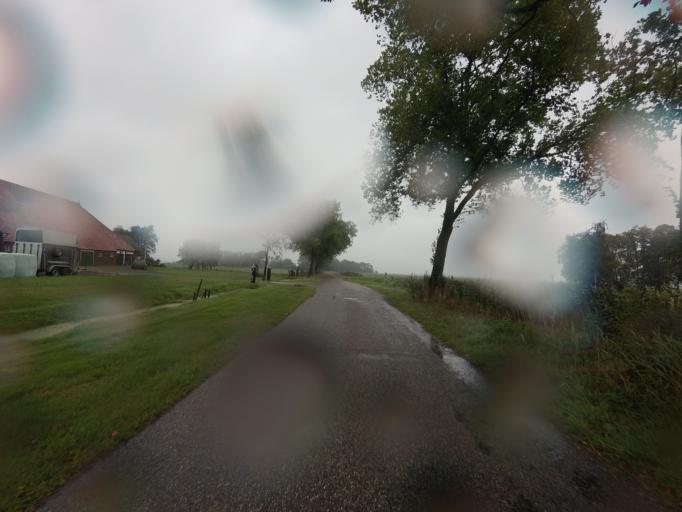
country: NL
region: Friesland
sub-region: Gemeente Boarnsterhim
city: Aldeboarn
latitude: 53.0712
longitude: 5.9289
